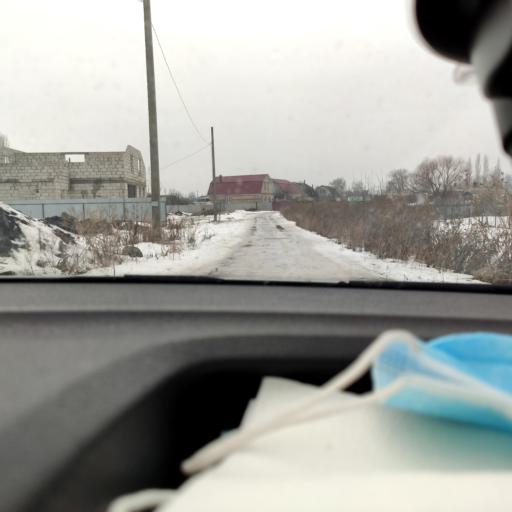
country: RU
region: Voronezj
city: Novaya Usman'
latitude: 51.6364
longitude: 39.3920
